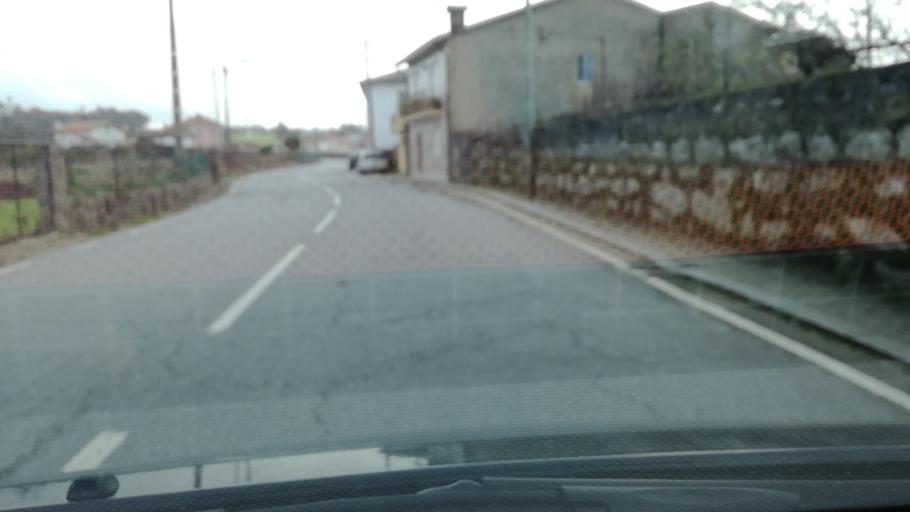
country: PT
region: Porto
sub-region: Maia
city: Gemunde
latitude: 41.2666
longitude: -8.6510
